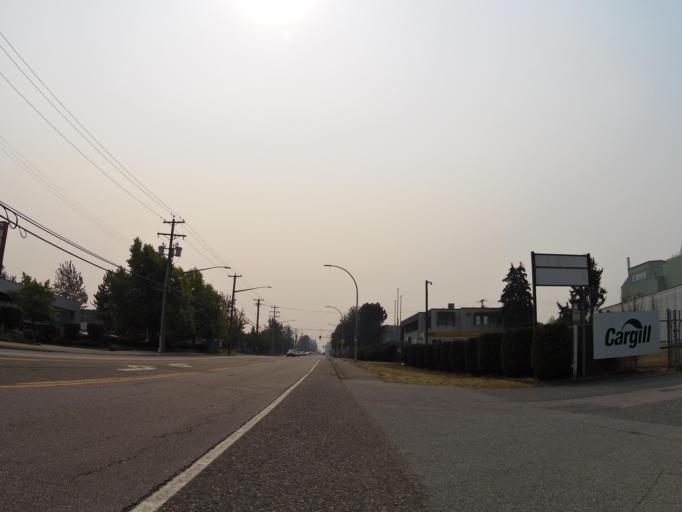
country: CA
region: British Columbia
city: Surrey
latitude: 49.1443
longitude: -122.8568
